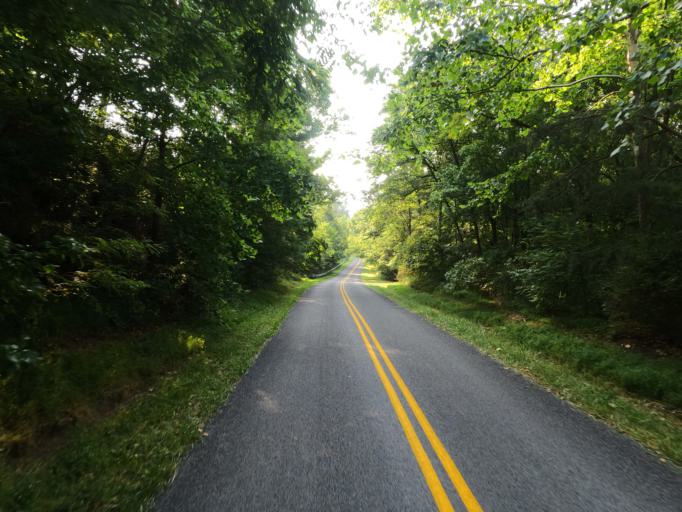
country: US
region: West Virginia
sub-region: Morgan County
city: Berkeley Springs
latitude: 39.6325
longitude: -78.3096
